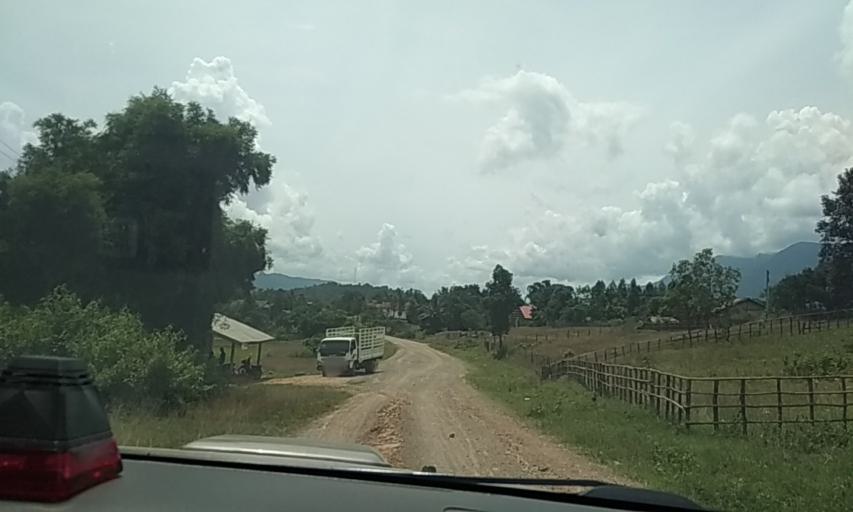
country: LA
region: Bolikhamxai
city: Ban Nahin
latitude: 18.1519
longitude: 104.7262
